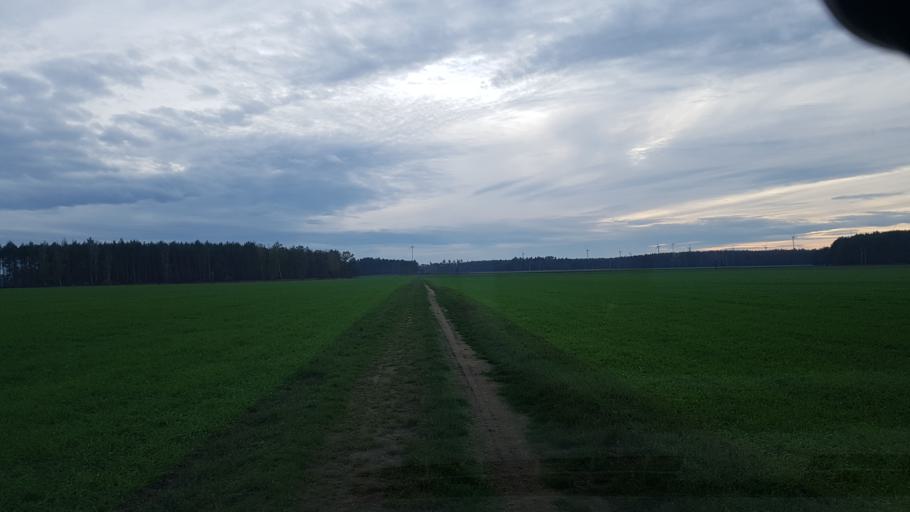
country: DE
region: Brandenburg
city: Falkenberg
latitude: 51.5388
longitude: 13.2719
